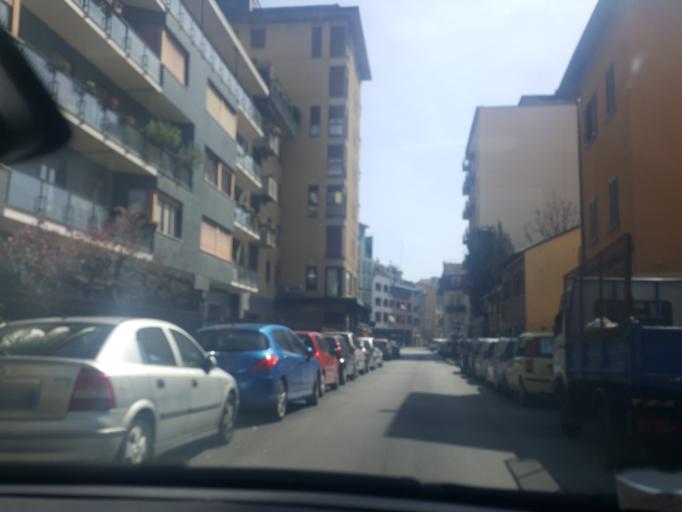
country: IT
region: Lombardy
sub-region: Citta metropolitana di Milano
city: Novate Milanese
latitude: 45.4933
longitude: 9.1498
